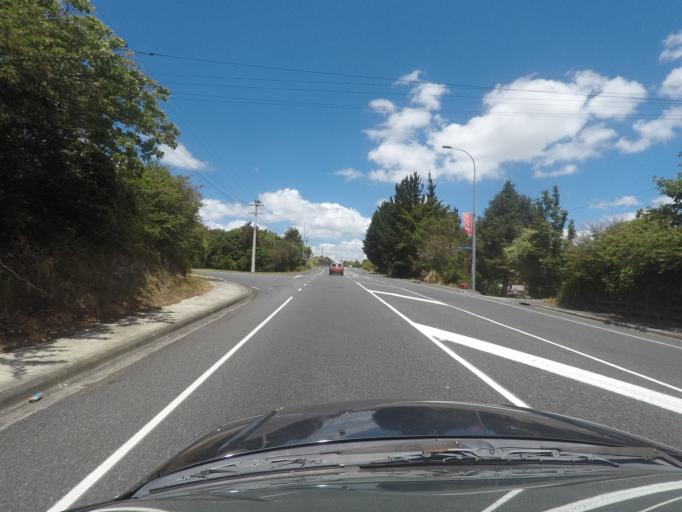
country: NZ
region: Northland
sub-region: Whangarei
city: Whangarei
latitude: -35.7452
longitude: 174.3667
